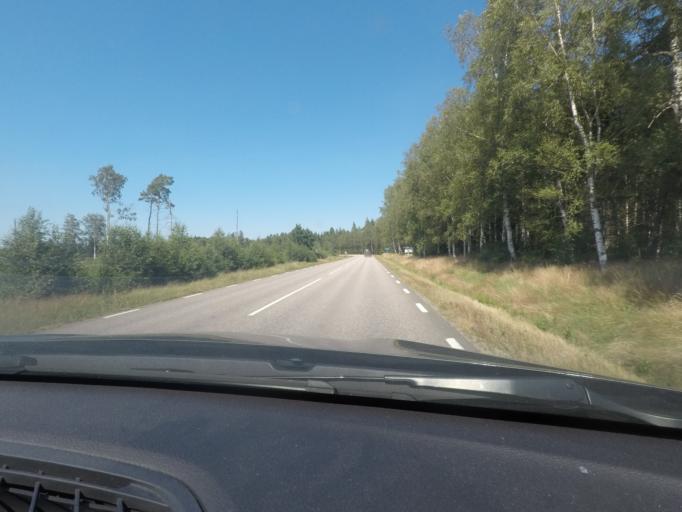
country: SE
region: Kronoberg
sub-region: Markaryds Kommun
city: Markaryd
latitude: 56.4821
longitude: 13.5320
